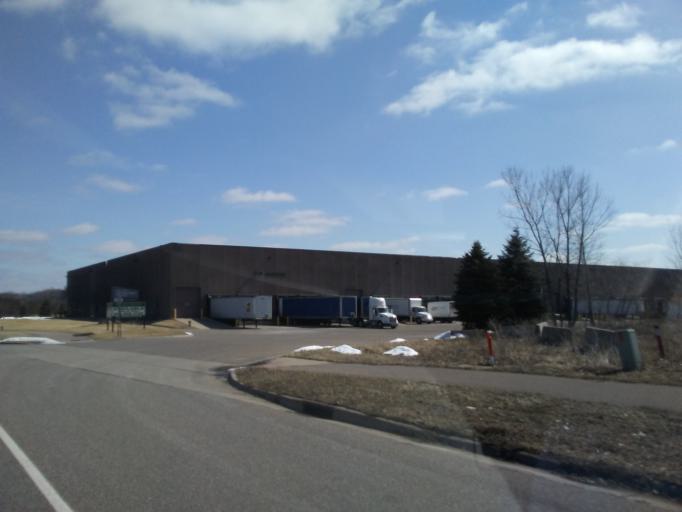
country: US
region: Minnesota
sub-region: Dakota County
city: Mendota Heights
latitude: 44.8342
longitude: -93.1140
